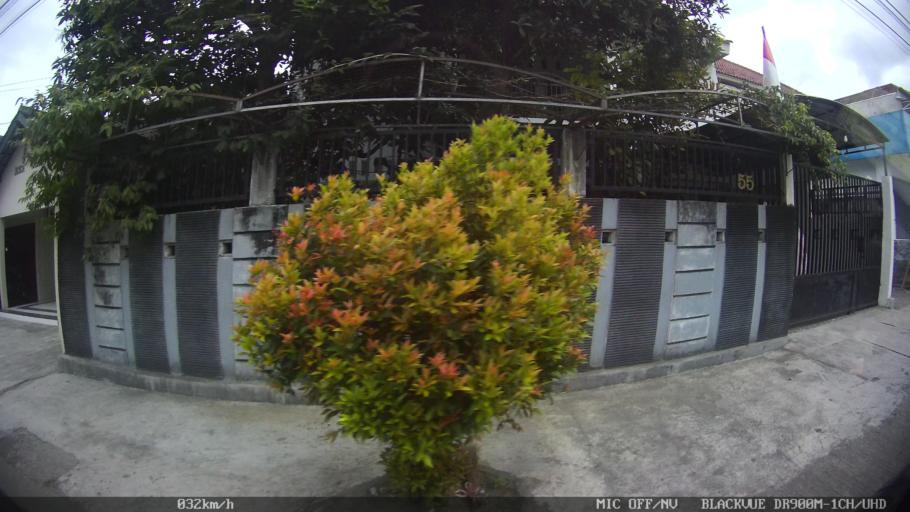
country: ID
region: Daerah Istimewa Yogyakarta
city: Depok
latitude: -7.8149
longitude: 110.4170
